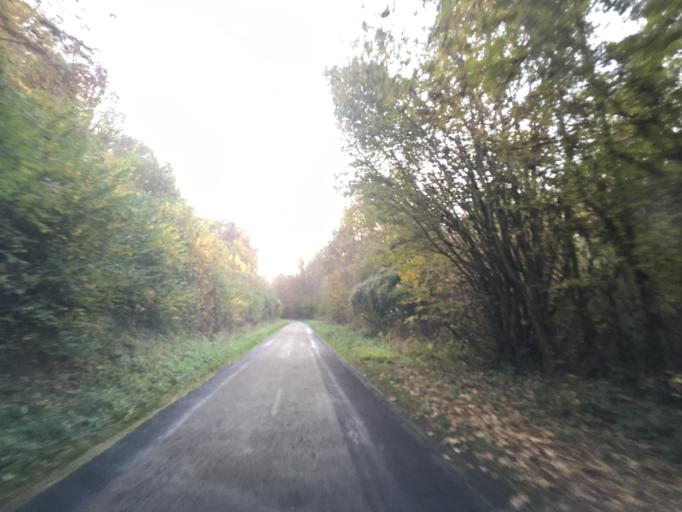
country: FR
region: Haute-Normandie
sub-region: Departement de l'Eure
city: Heudreville-sur-Eure
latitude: 49.1053
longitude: 1.2248
